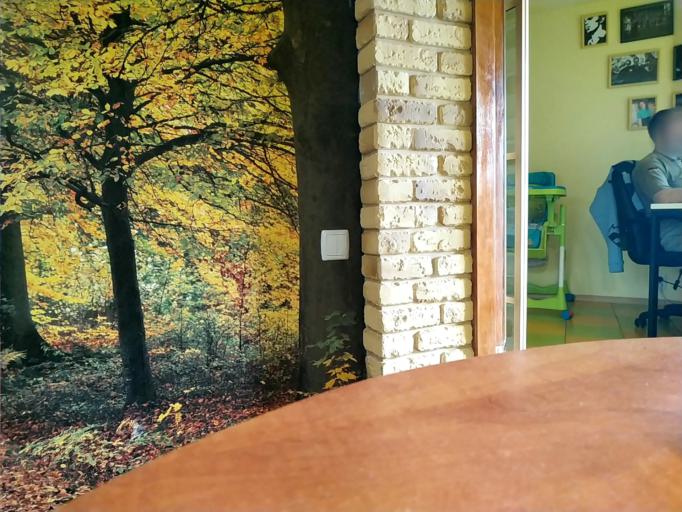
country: RU
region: Tverskaya
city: Vasil'yevskiy Mokh
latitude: 57.2110
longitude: 35.7290
